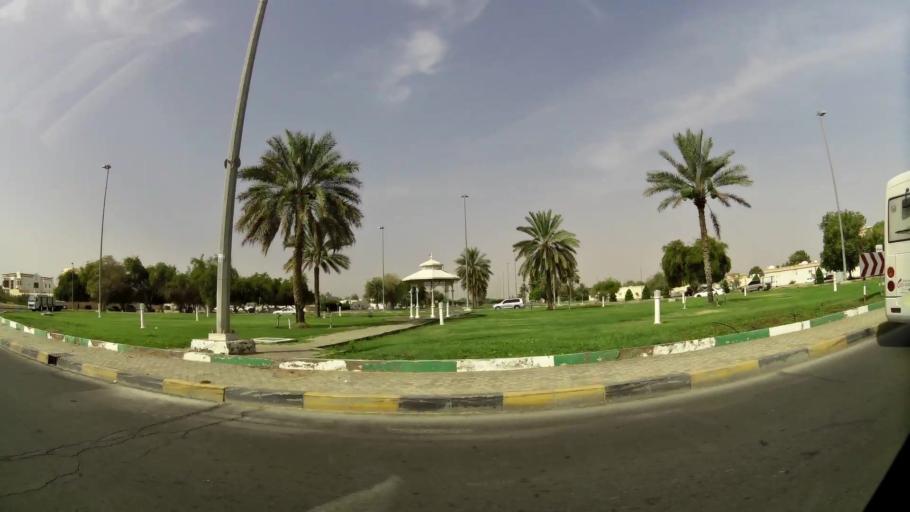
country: AE
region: Abu Dhabi
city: Al Ain
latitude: 24.1511
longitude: 55.6955
